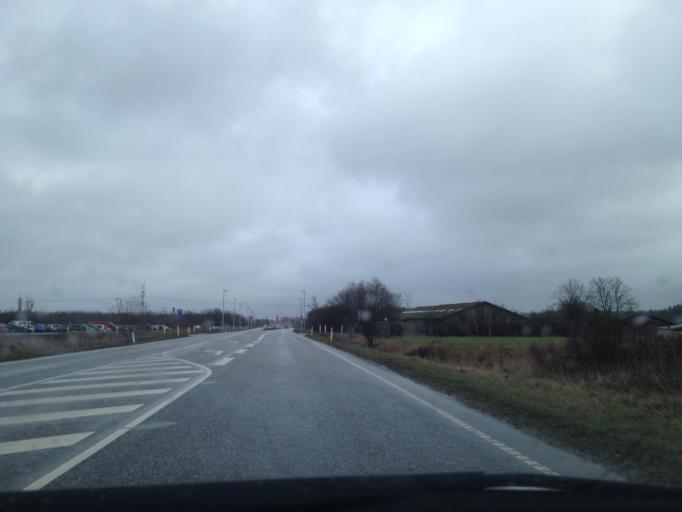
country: DK
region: South Denmark
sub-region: Kolding Kommune
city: Kolding
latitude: 55.4655
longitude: 9.4324
